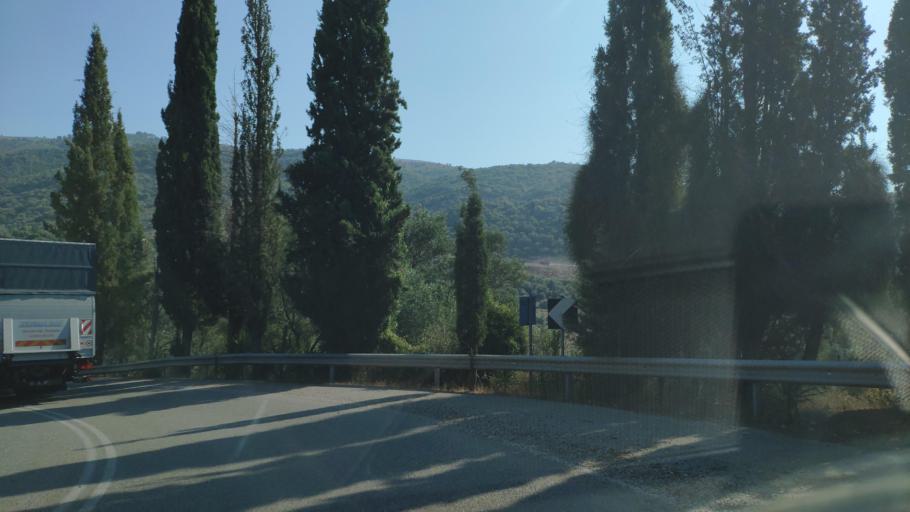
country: GR
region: West Greece
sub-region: Nomos Aitolias kai Akarnanias
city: Stanos
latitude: 38.7729
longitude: 21.1487
